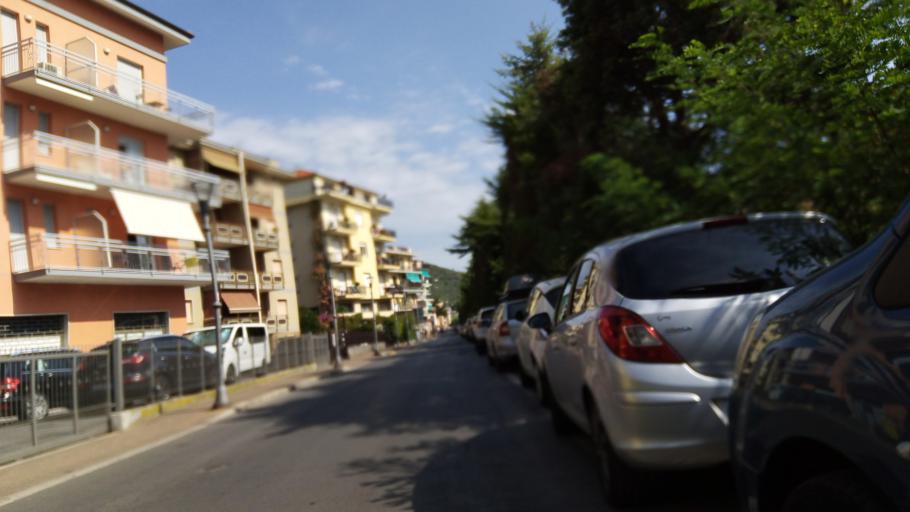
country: IT
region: Liguria
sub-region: Provincia di Savona
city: Ceriale
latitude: 44.0883
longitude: 8.2288
